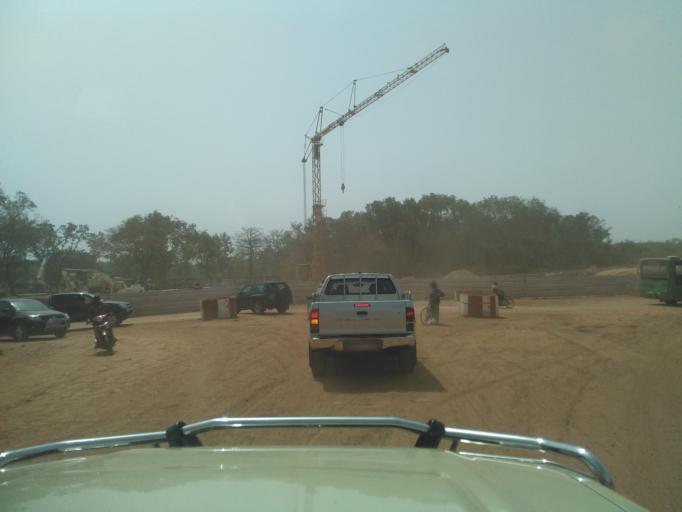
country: BF
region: Centre
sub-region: Kadiogo Province
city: Ouagadougou
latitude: 12.3854
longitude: -1.5025
